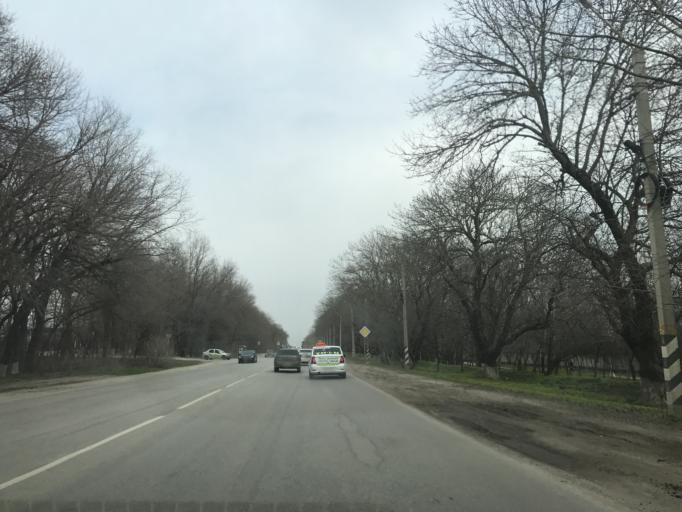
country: RU
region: Rostov
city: Aksay
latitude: 47.2761
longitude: 39.8864
